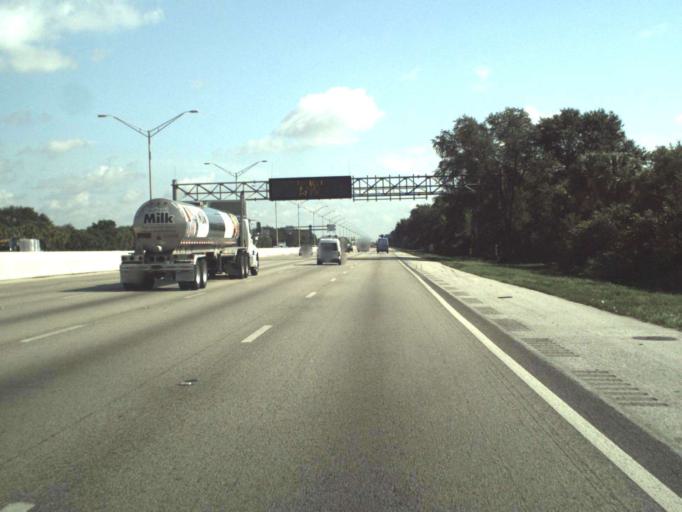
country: US
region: Florida
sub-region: Palm Beach County
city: Schall Circle
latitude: 26.7336
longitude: -80.0908
